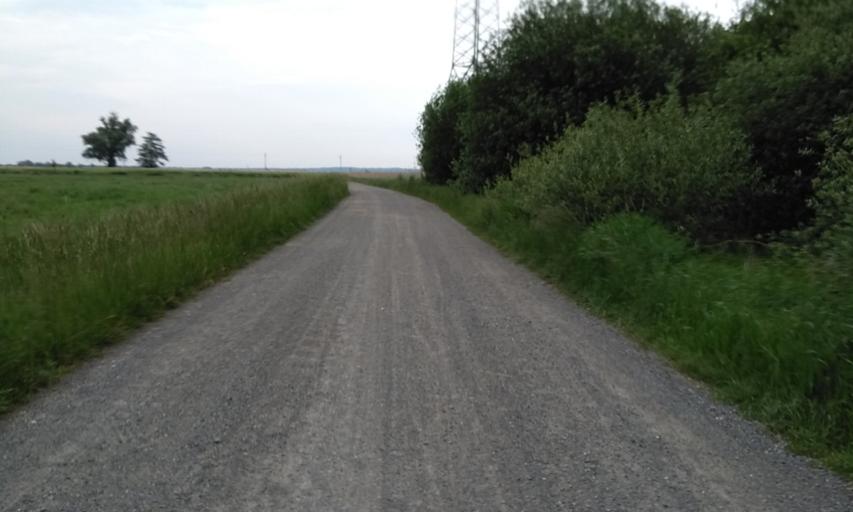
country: DE
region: Lower Saxony
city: Buxtehude
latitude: 53.4925
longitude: 9.6855
